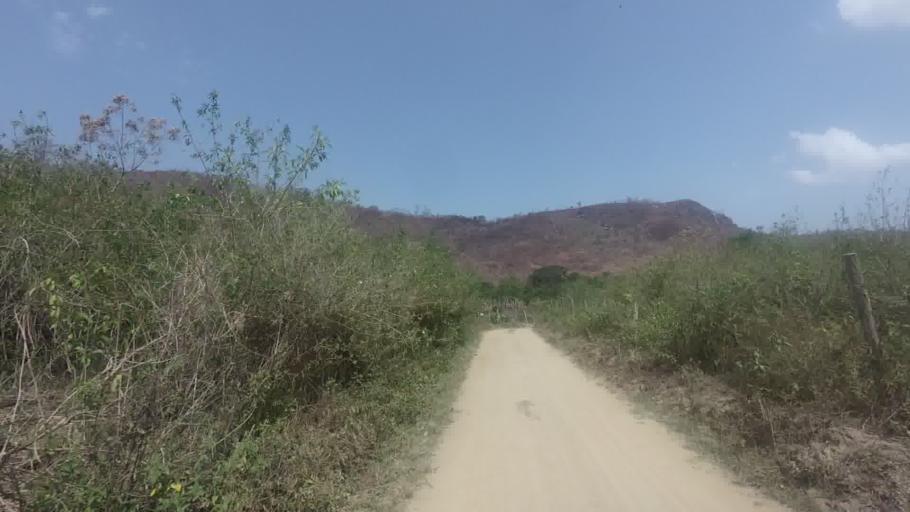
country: BR
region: Espirito Santo
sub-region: Sao Jose Do Calcado
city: Sao Jose do Calcado
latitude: -21.0272
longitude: -41.5168
